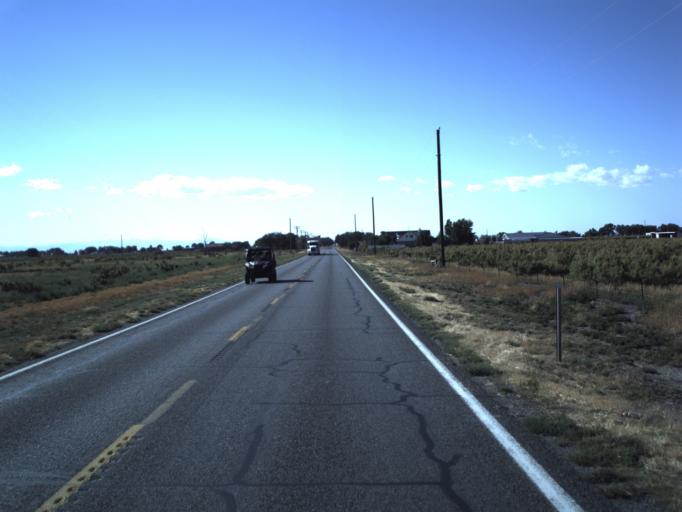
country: US
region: Utah
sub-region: Millard County
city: Delta
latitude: 39.3051
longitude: -112.6526
